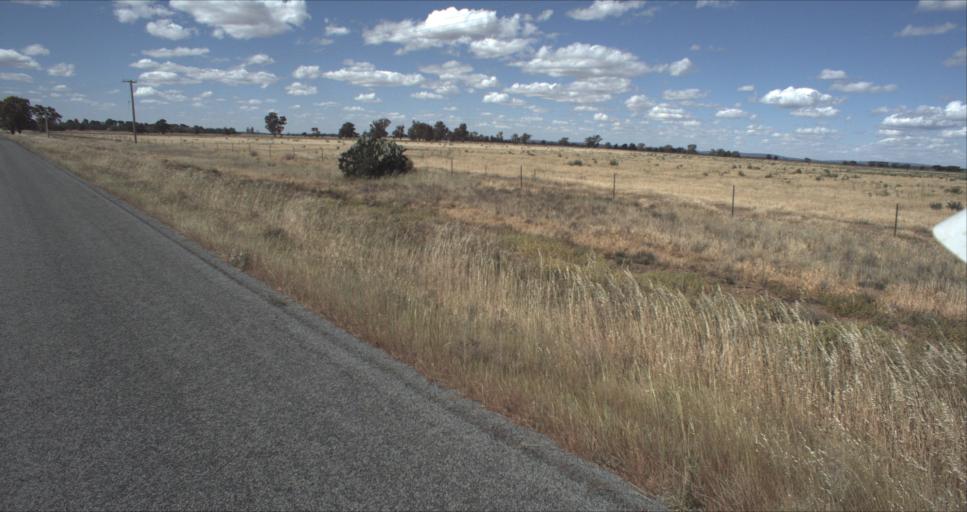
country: AU
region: New South Wales
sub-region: Leeton
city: Leeton
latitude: -34.4961
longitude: 146.2463
